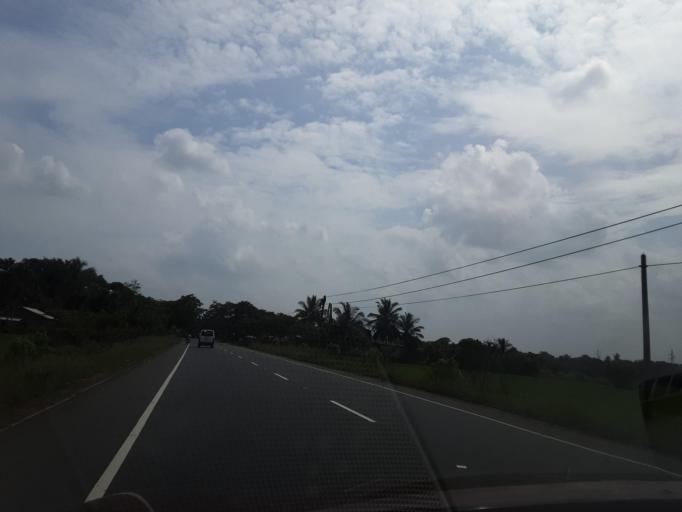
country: LK
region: North Central
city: Anuradhapura
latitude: 8.5067
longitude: 80.5077
